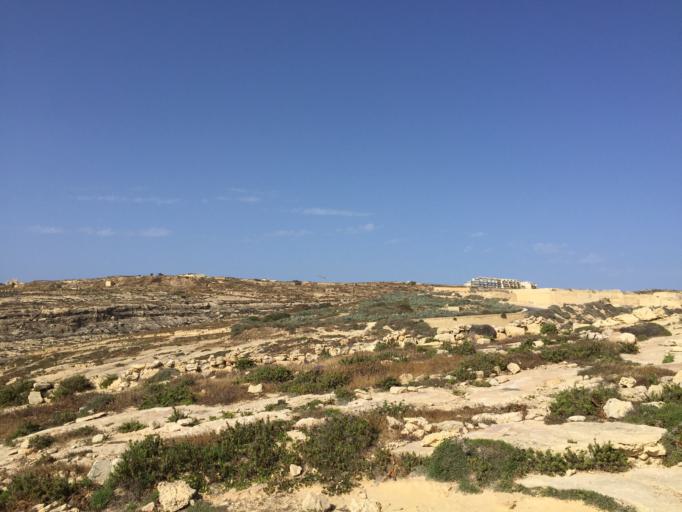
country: MT
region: Saint Lawrence
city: San Lawrenz
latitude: 36.0489
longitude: 14.1930
